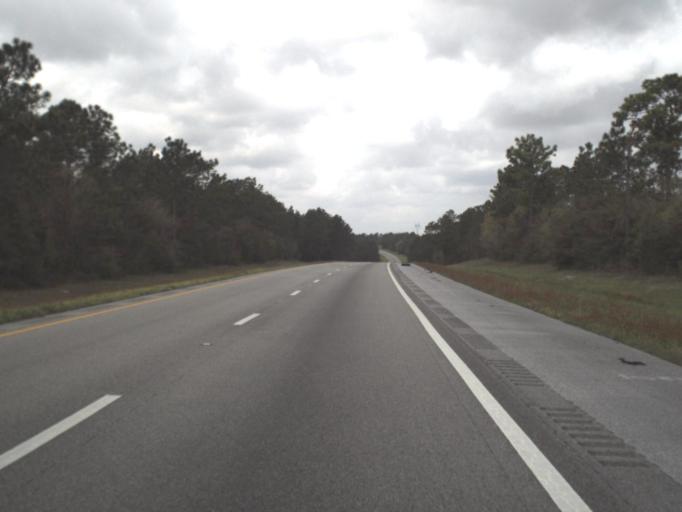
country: US
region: Florida
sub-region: Okaloosa County
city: Crestview
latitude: 30.7219
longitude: -86.4778
